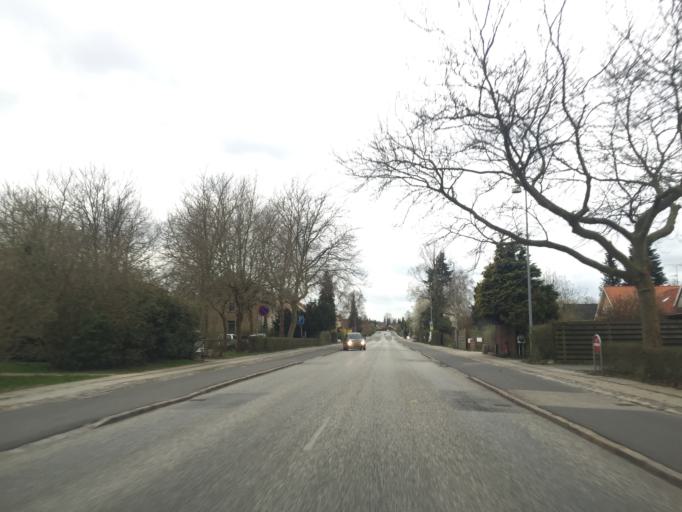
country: DK
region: Capital Region
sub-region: Rudersdal Kommune
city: Holte
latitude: 55.7949
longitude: 12.4688
